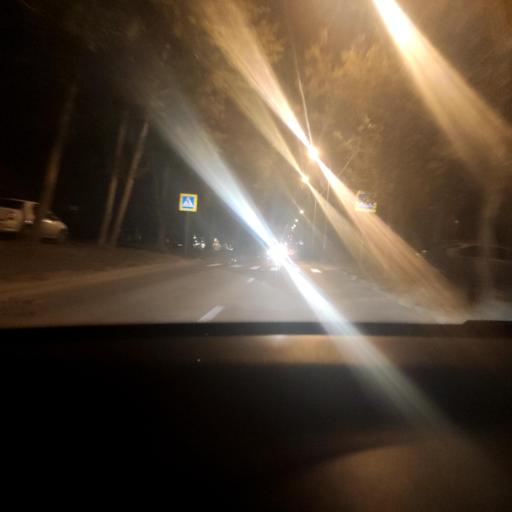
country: RU
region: Samara
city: Samara
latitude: 53.2262
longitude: 50.2135
